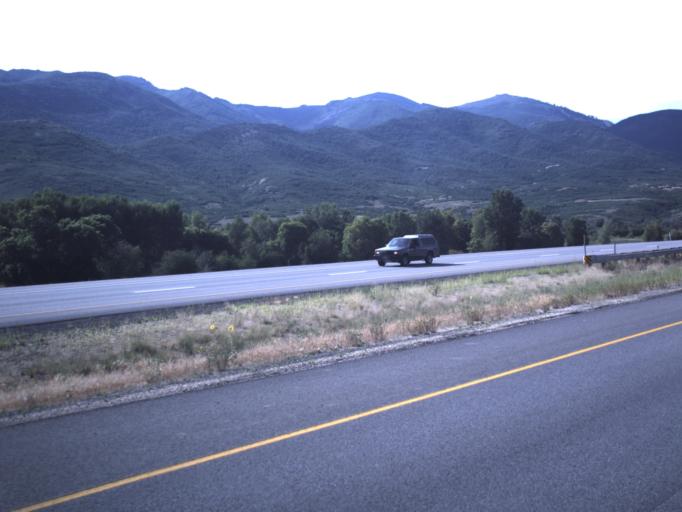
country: US
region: Utah
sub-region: Wasatch County
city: Heber
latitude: 40.5618
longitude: -111.4276
